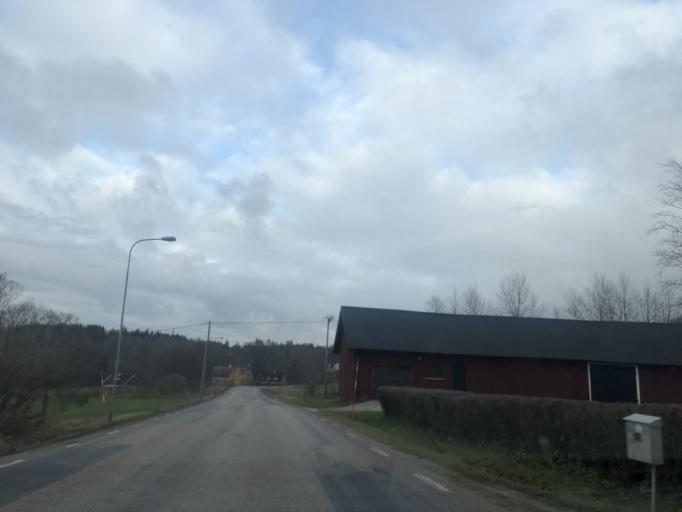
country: SE
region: Vaestra Goetaland
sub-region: Tranemo Kommun
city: Langhem
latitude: 57.7174
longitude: 13.3004
